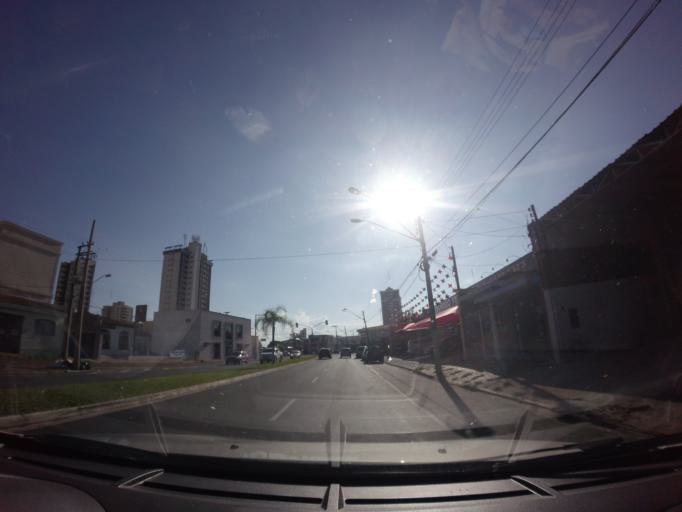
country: BR
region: Sao Paulo
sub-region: Rio Claro
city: Rio Claro
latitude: -22.4109
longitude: -47.5672
